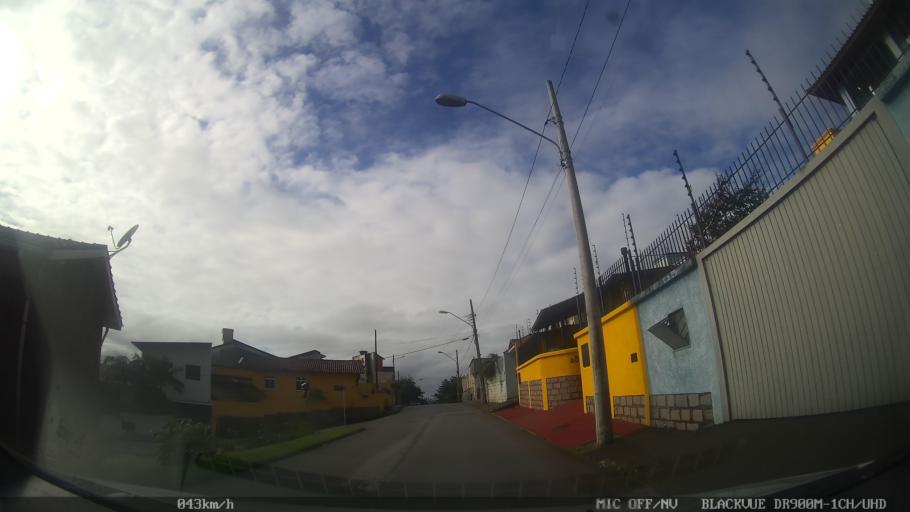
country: BR
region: Santa Catarina
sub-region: Sao Jose
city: Campinas
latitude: -27.6134
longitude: -48.6284
